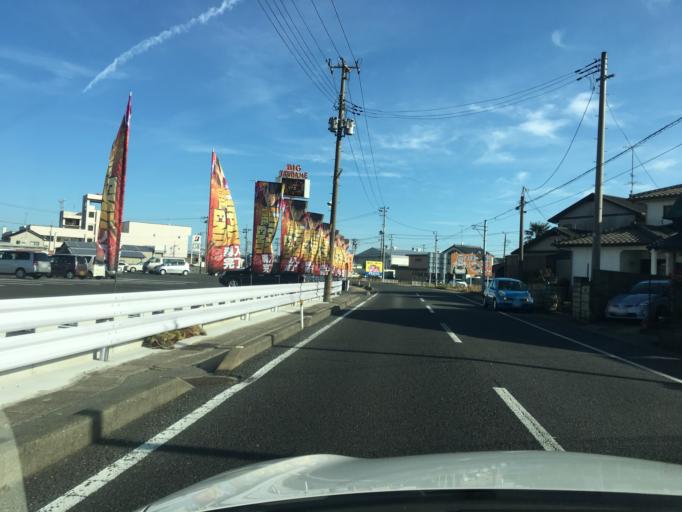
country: JP
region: Fukushima
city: Iwaki
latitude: 36.9491
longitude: 140.8846
